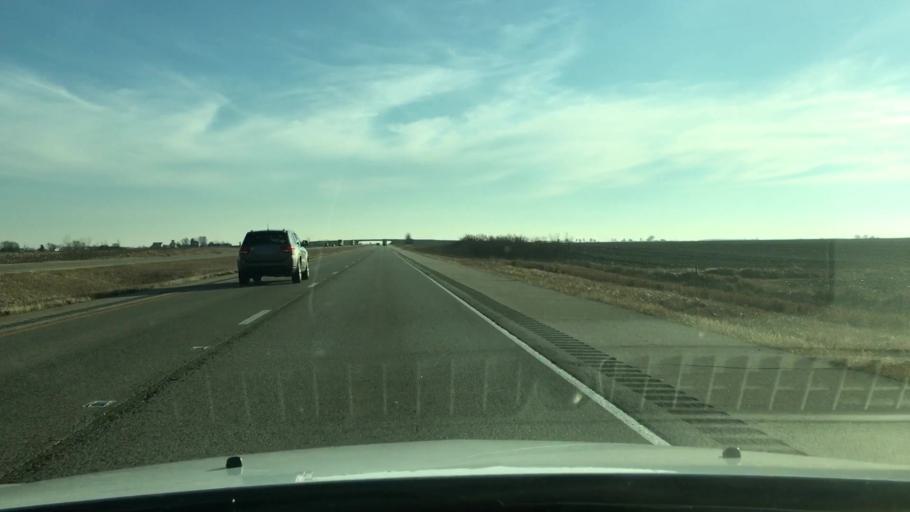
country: US
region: Illinois
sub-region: Woodford County
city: Minonk
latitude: 40.8366
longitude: -89.0363
